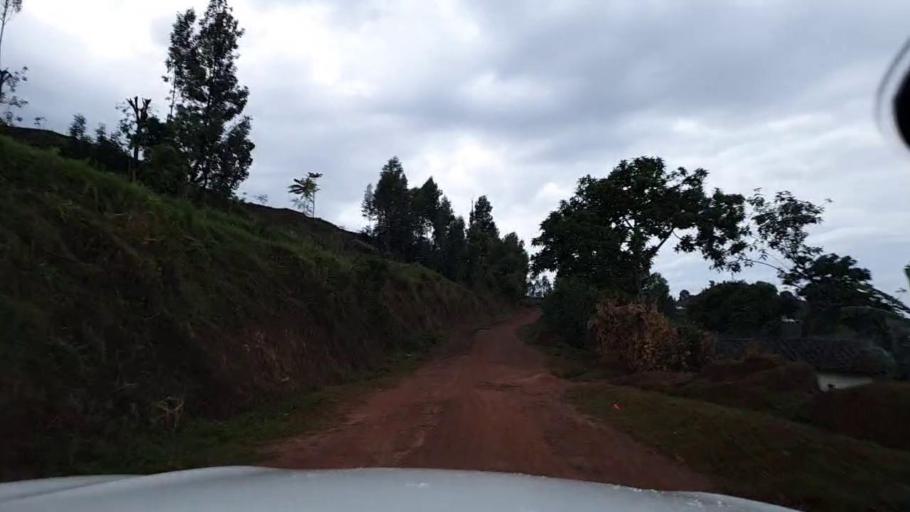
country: BI
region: Kayanza
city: Kayanza
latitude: -2.7160
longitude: 29.5426
